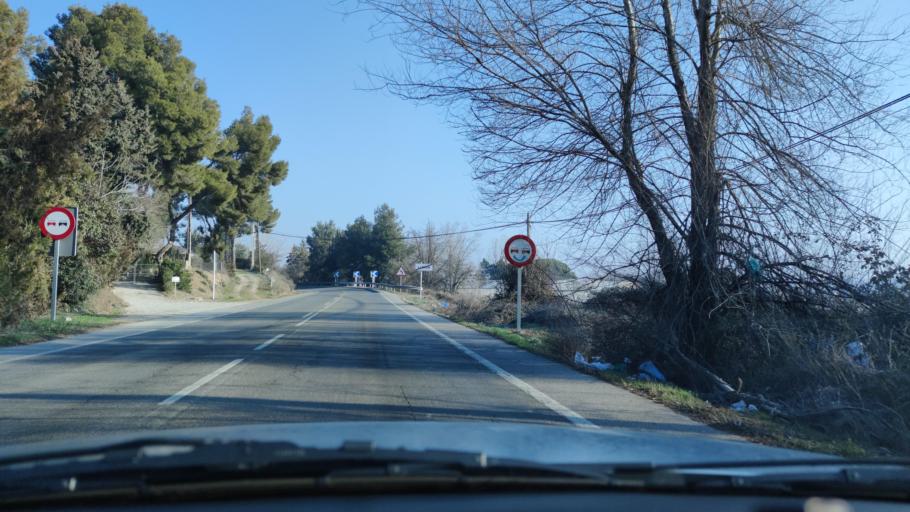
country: ES
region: Catalonia
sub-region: Provincia de Lleida
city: Lleida
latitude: 41.6318
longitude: 0.6348
